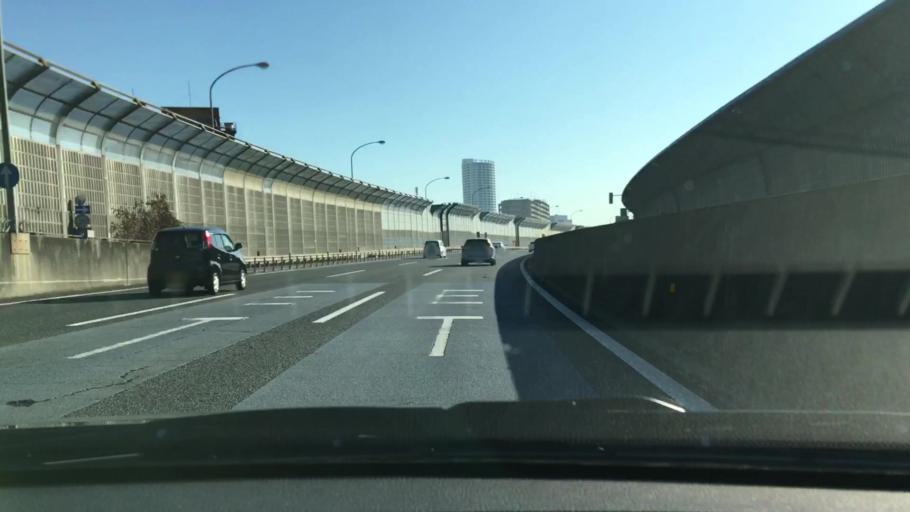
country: JP
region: Chiba
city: Funabashi
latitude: 35.6989
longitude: 139.9693
